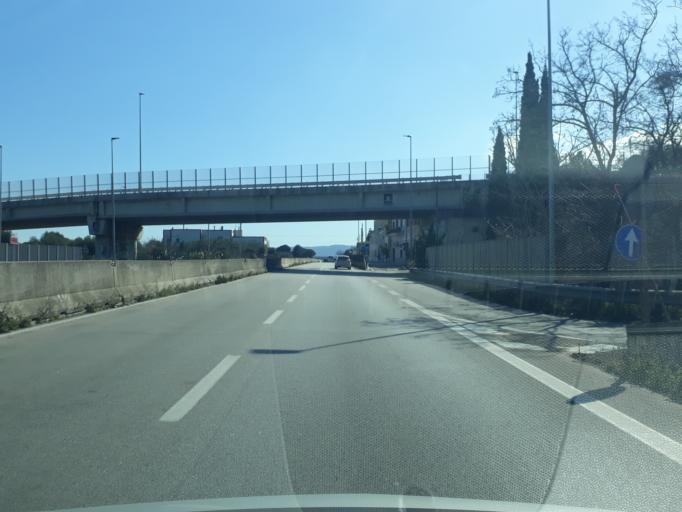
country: IT
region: Apulia
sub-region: Provincia di Brindisi
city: Fasano
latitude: 40.8807
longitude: 17.3380
